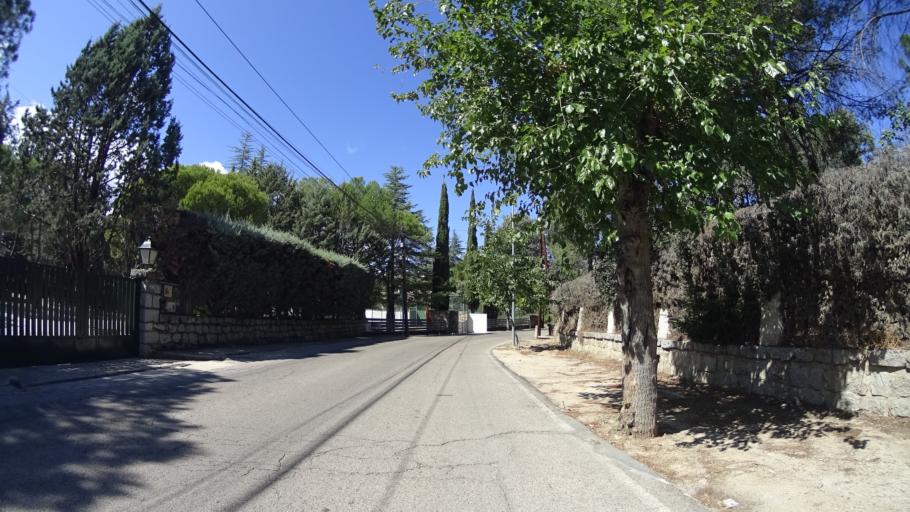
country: ES
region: Madrid
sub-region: Provincia de Madrid
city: Torrelodones
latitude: 40.5693
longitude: -3.9506
